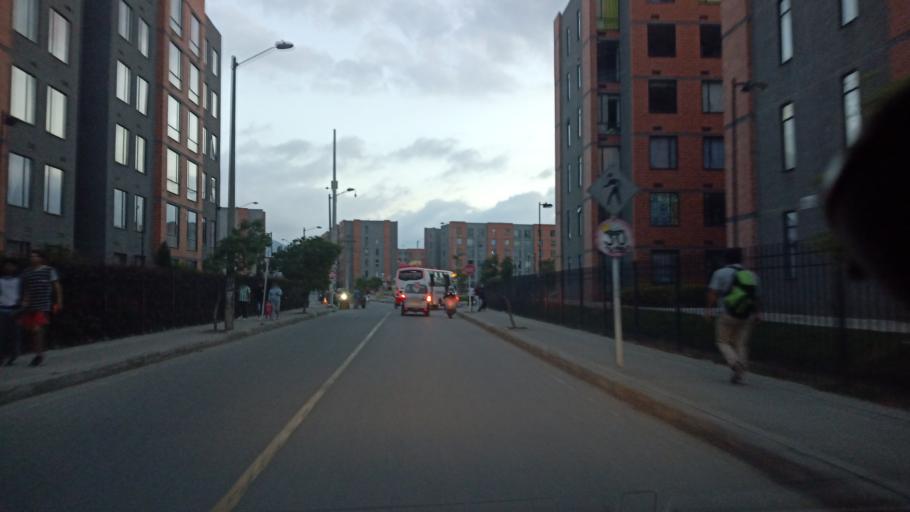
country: CO
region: Cundinamarca
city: Soacha
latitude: 4.5807
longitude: -74.2310
